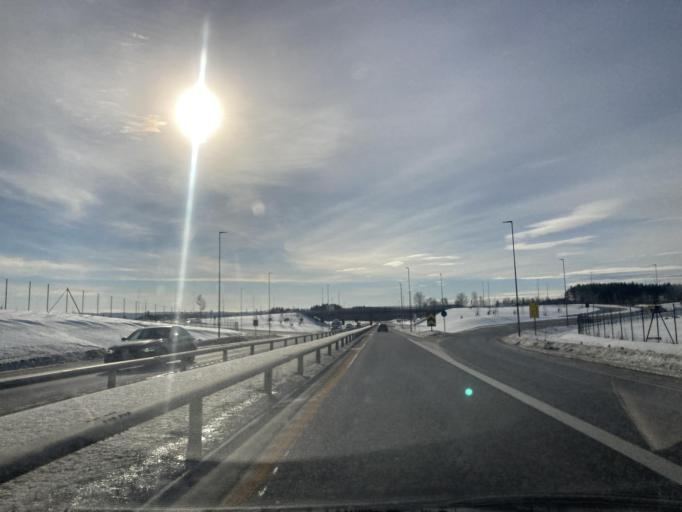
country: NO
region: Hedmark
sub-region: Loten
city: Loten
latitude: 60.8289
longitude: 11.2928
